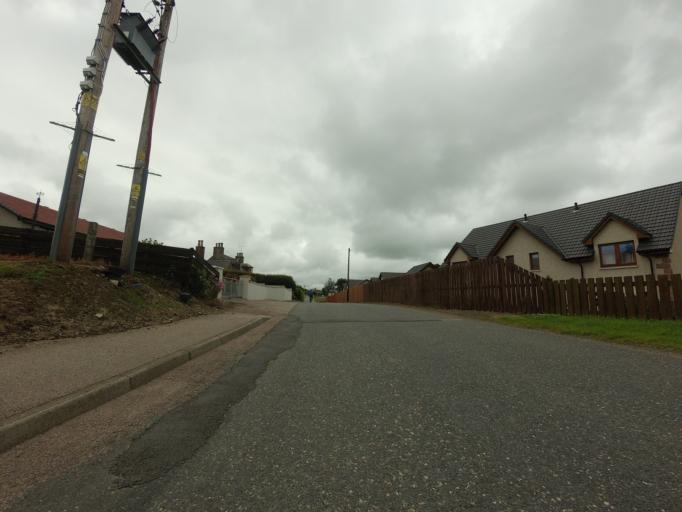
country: GB
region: Scotland
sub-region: Aberdeenshire
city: Turriff
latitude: 57.5356
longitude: -2.4422
